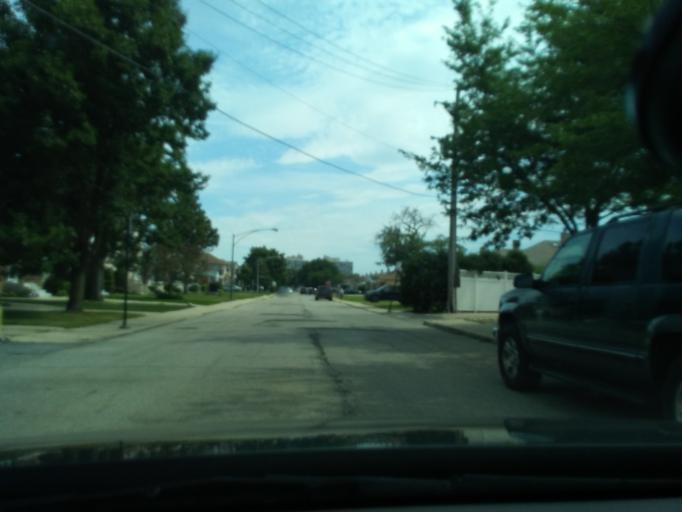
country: US
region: Illinois
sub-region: Cook County
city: Harwood Heights
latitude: 41.9747
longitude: -87.8059
